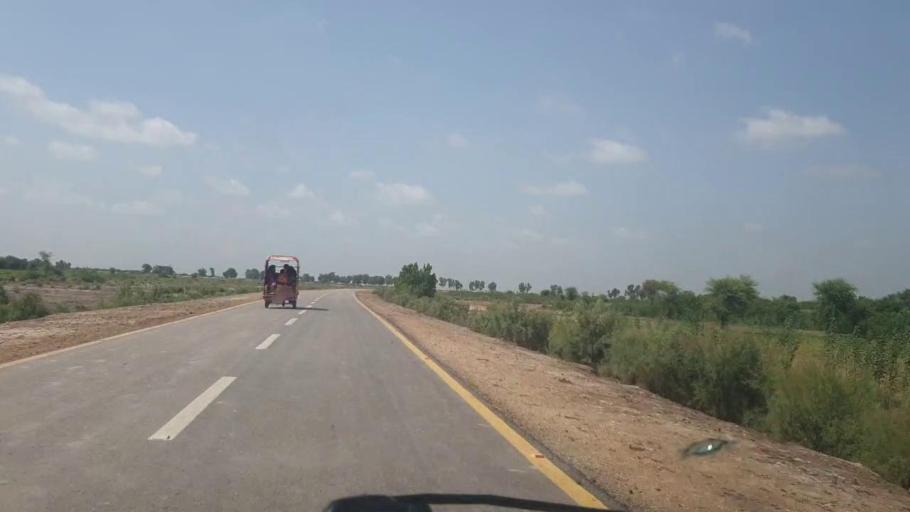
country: PK
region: Sindh
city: Berani
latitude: 25.7082
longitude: 68.9421
